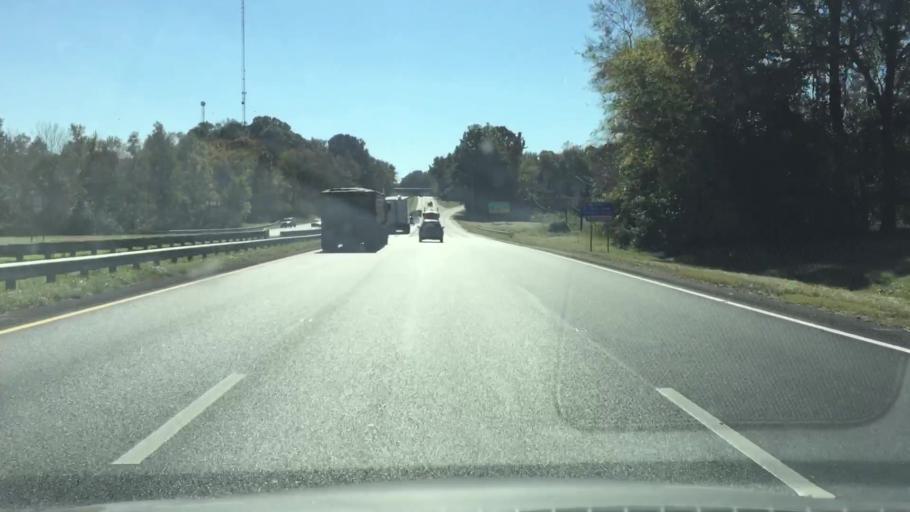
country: US
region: North Carolina
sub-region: Guilford County
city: Greensboro
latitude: 36.1060
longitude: -79.7613
